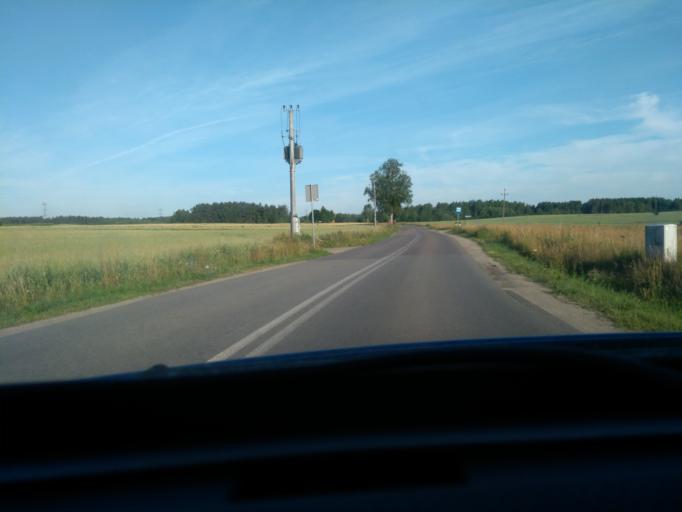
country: PL
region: Pomeranian Voivodeship
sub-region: Powiat kartuski
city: Banino
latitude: 54.3923
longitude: 18.3565
